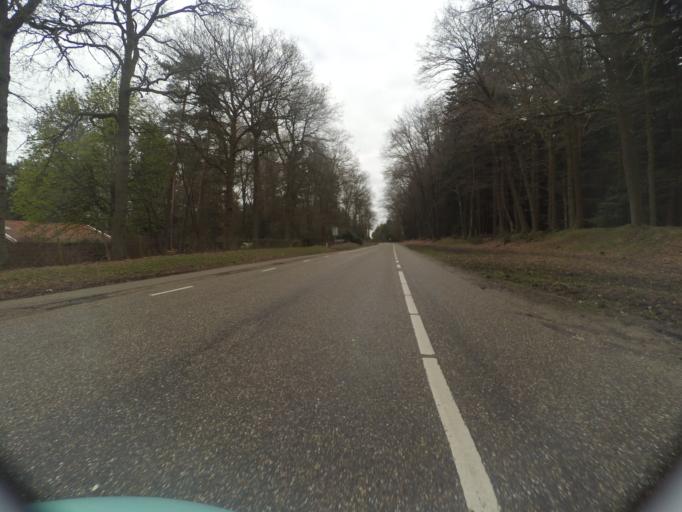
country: NL
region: Gelderland
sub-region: Gemeente Apeldoorn
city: Beekbergen
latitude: 52.1071
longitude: 5.9523
